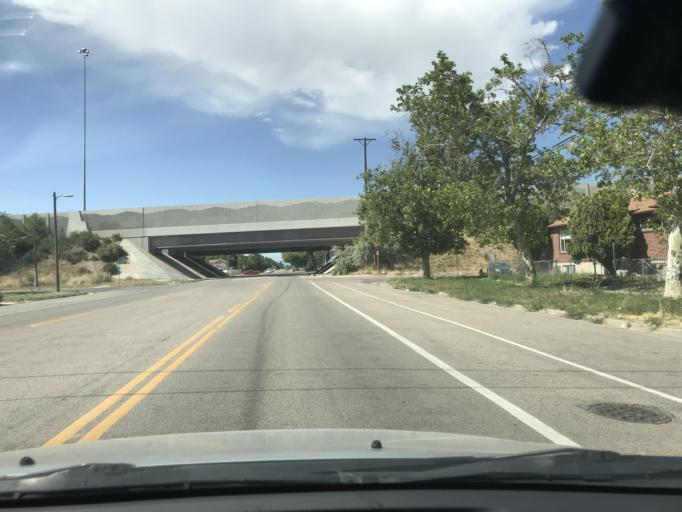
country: US
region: Utah
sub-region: Salt Lake County
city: Salt Lake City
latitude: 40.7633
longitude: -111.9196
